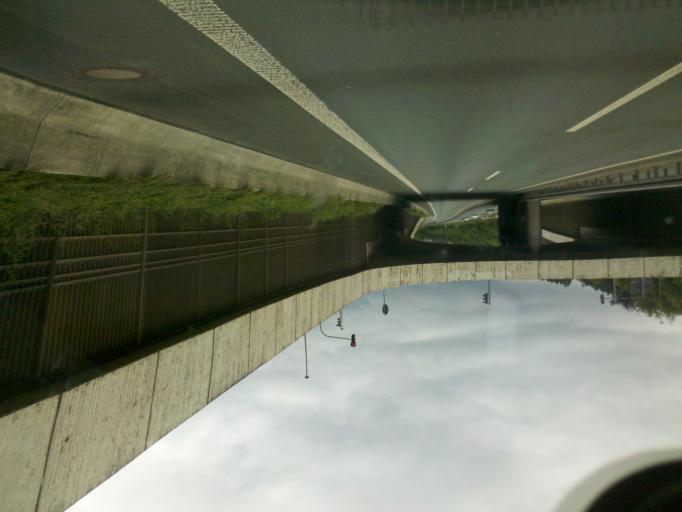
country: DE
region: North Rhine-Westphalia
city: Kreuztal
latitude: 50.9347
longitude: 8.0099
